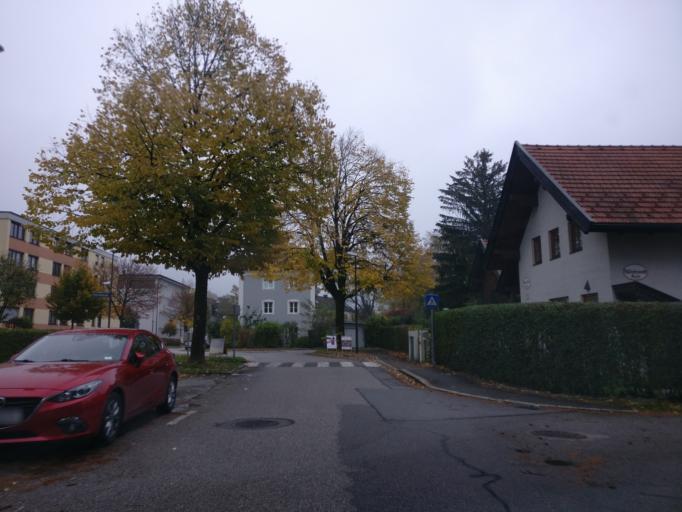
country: AT
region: Salzburg
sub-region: Salzburg Stadt
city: Salzburg
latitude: 47.7827
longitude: 13.0641
